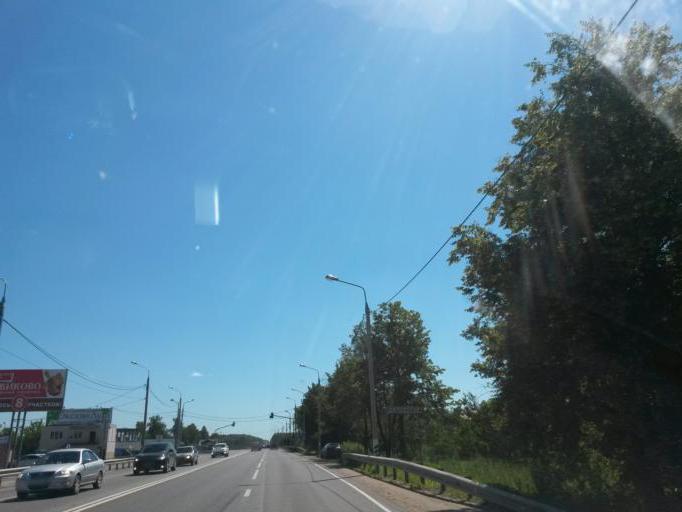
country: RU
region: Moskovskaya
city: Proletarskiy
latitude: 55.0285
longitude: 37.4275
